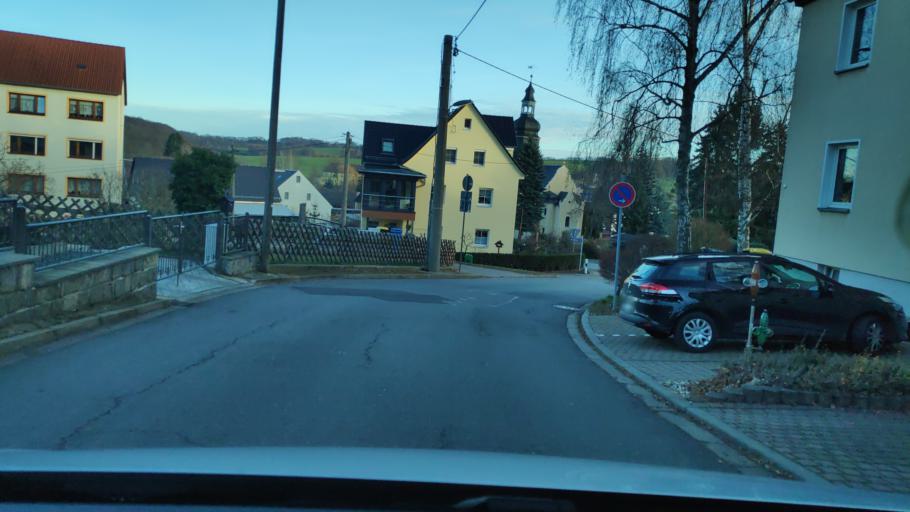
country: DE
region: Saxony
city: Mulsen
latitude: 50.7484
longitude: 12.5687
